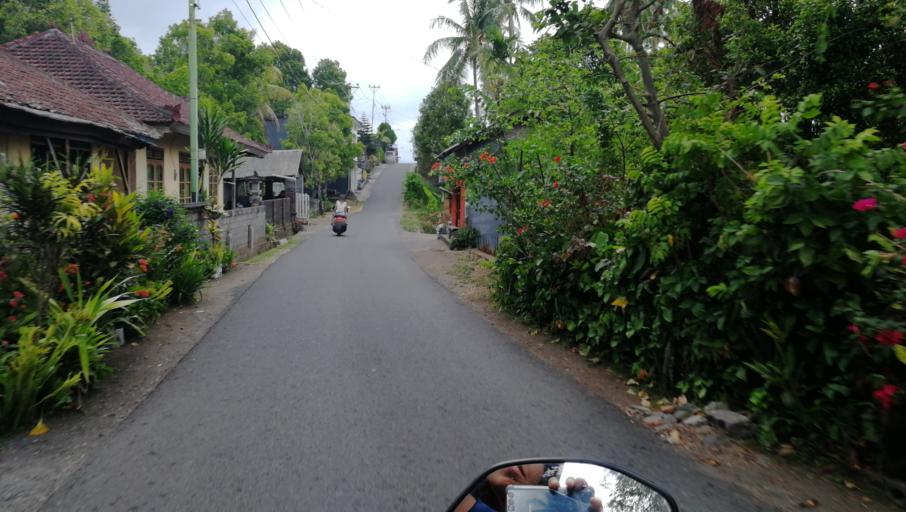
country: ID
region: Bali
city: Puspajati
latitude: -8.2727
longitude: 115.0209
